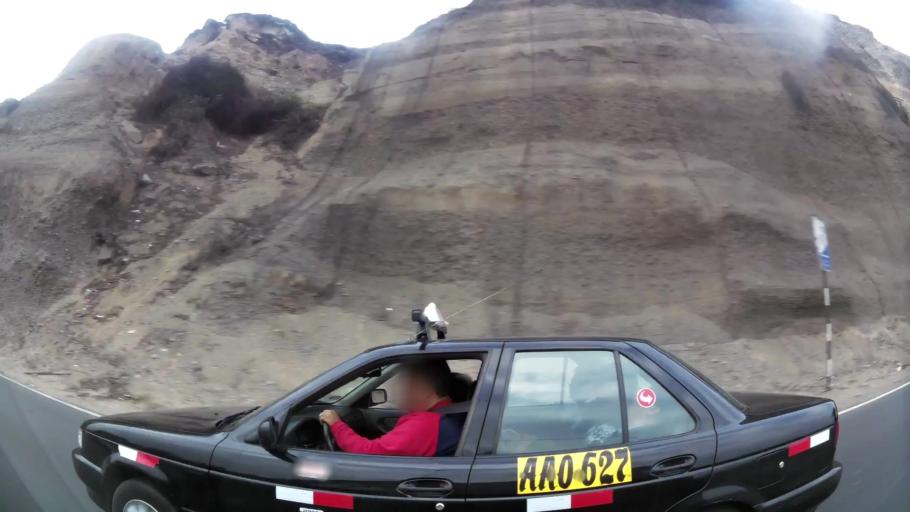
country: PE
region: Lima
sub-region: Lima
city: Surco
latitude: -12.1616
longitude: -77.0248
